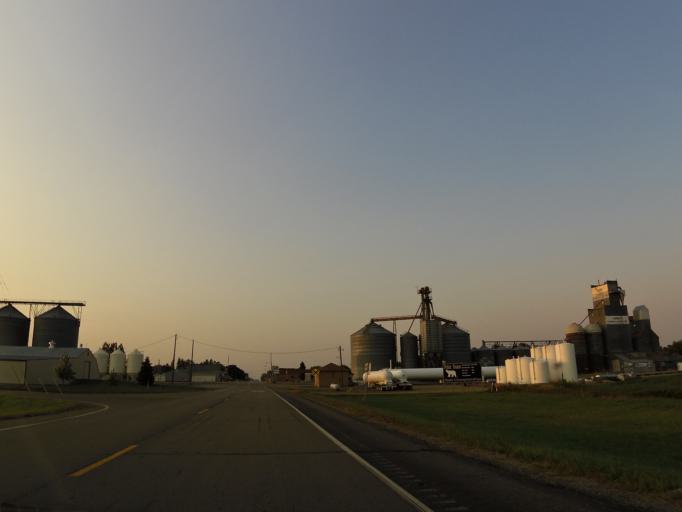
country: US
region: North Dakota
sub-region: Grand Forks County
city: Larimore
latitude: 47.9020
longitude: -97.6237
